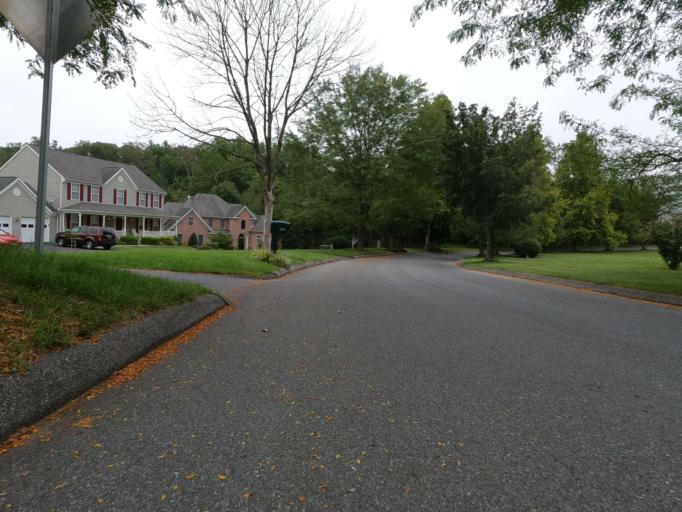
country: US
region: Maryland
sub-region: Carroll County
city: Sykesville
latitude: 39.3354
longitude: -77.0483
